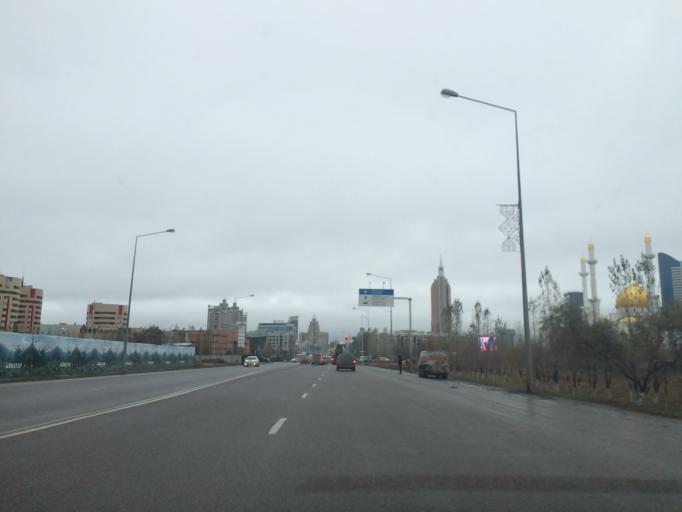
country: KZ
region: Astana Qalasy
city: Astana
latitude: 51.1240
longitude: 71.4128
